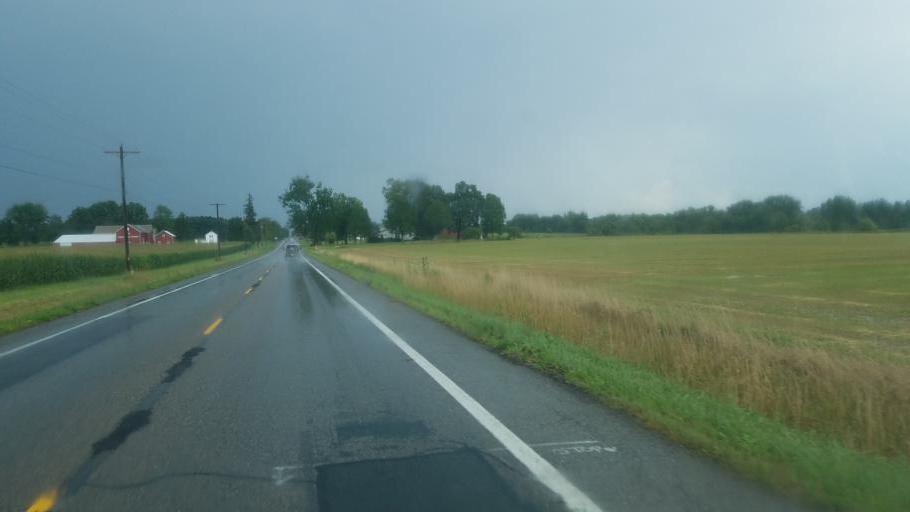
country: US
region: Ohio
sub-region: Ashtabula County
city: Orwell
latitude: 41.4618
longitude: -80.8884
